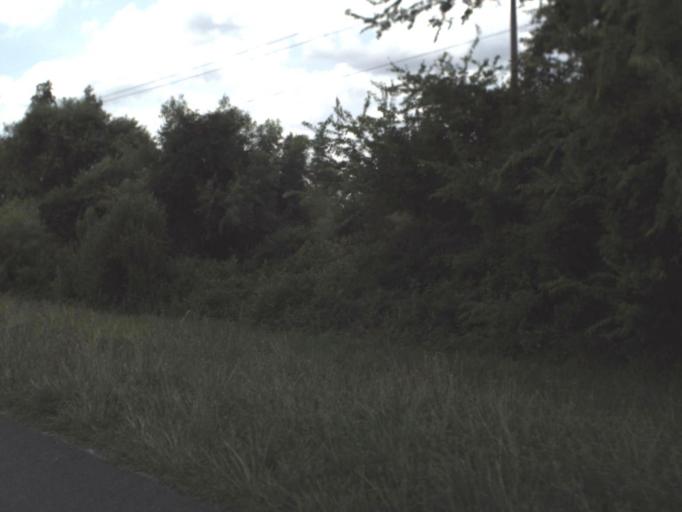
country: US
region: Florida
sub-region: Hamilton County
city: Jasper
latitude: 30.4444
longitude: -82.8803
